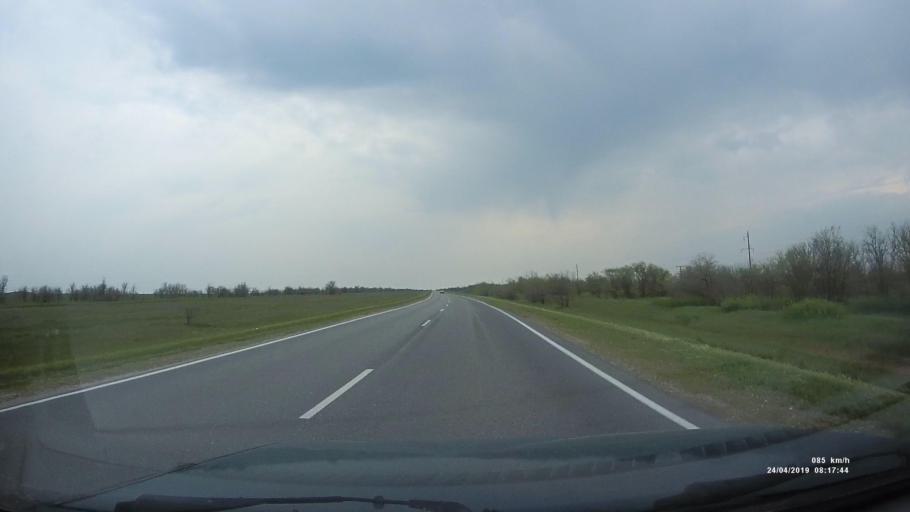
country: RU
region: Kalmykiya
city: Priyutnoye
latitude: 46.0982
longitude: 43.6359
